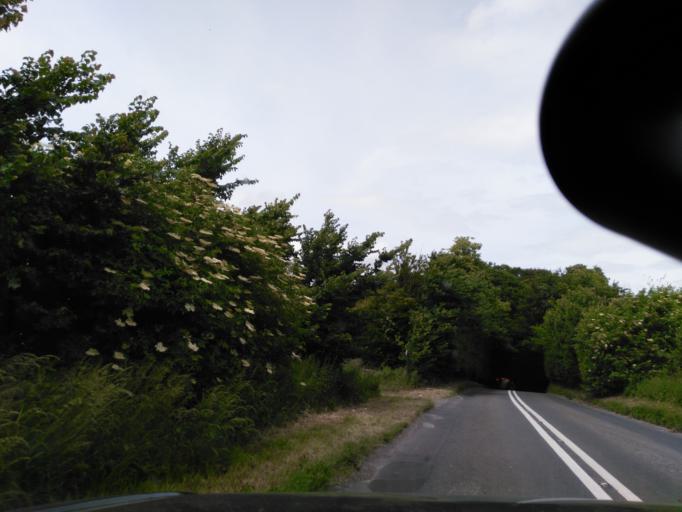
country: GB
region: England
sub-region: Wiltshire
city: Market Lavington
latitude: 51.2609
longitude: -1.9890
